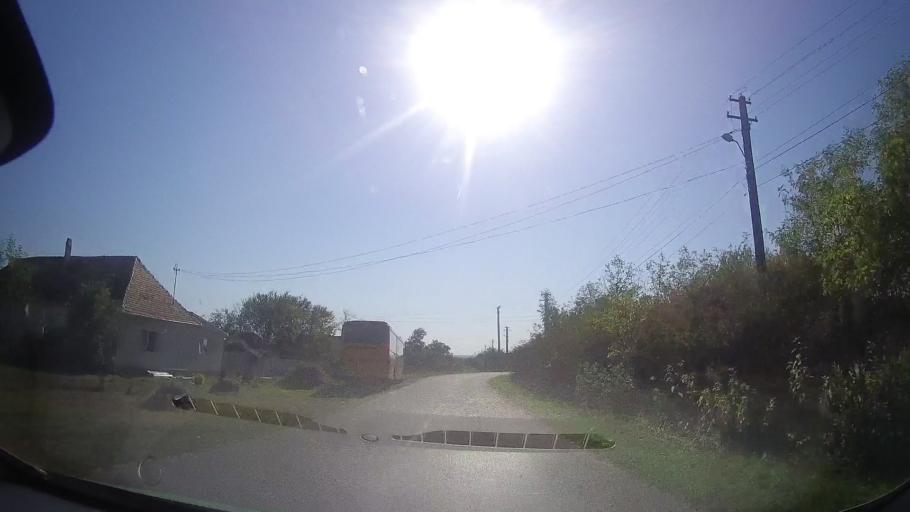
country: RO
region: Timis
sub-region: Comuna Ghizela
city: Ghizela
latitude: 45.8254
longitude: 21.7516
